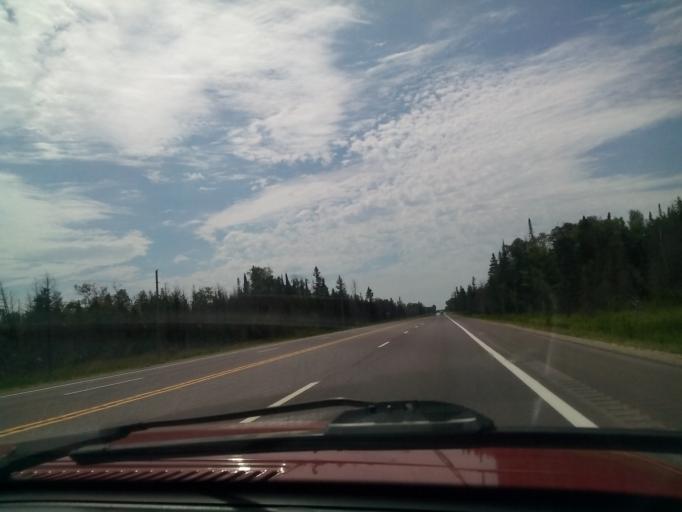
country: US
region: Michigan
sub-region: Schoolcraft County
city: Manistique
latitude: 46.0246
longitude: -85.9850
